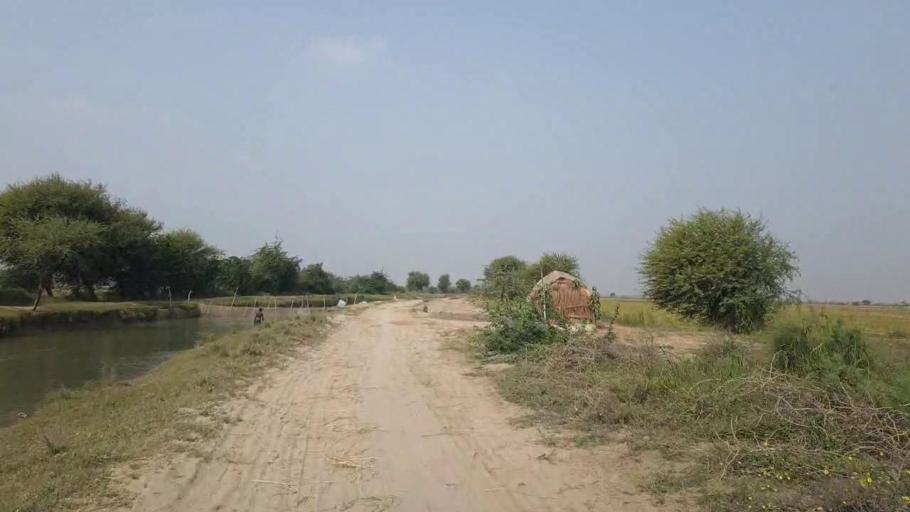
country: PK
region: Sindh
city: Kario
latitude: 24.8413
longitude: 68.5384
